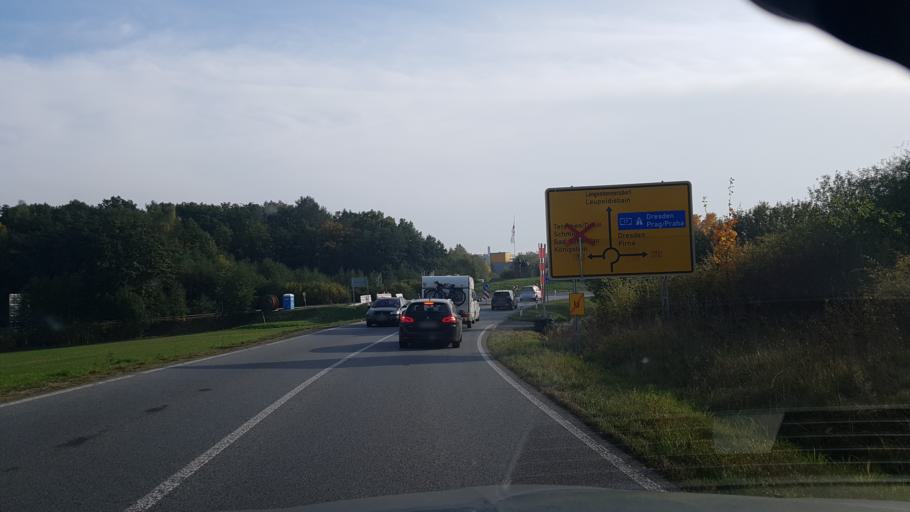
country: DE
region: Saxony
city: Struppen
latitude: 50.9207
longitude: 14.0251
